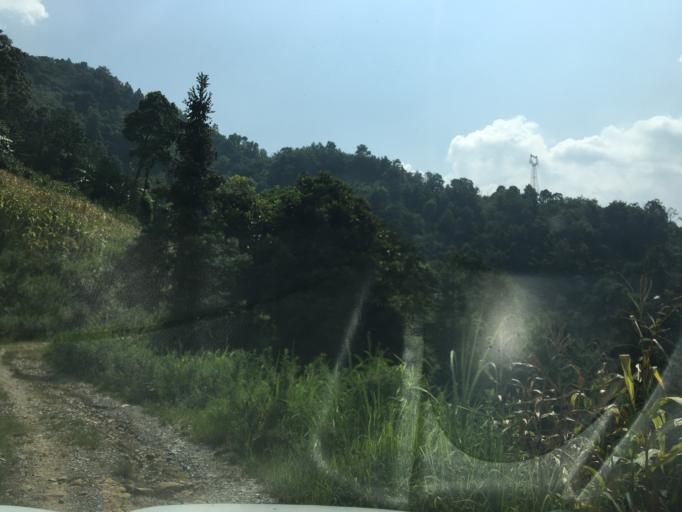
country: CN
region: Guangxi Zhuangzu Zizhiqu
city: Xinzhou
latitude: 24.9903
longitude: 105.7428
